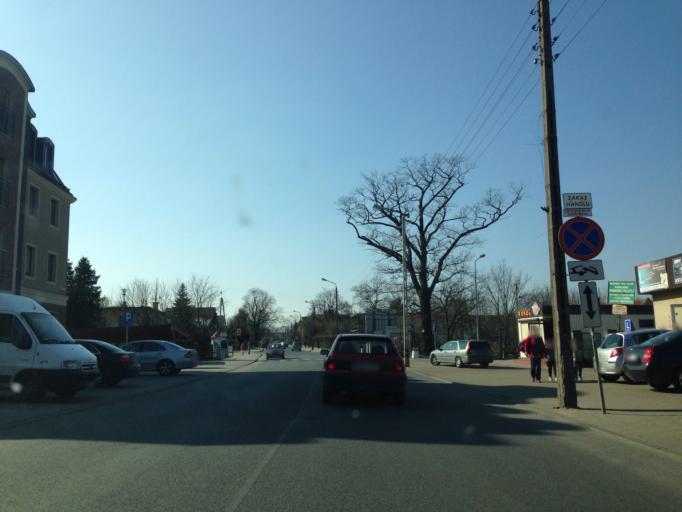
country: PL
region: Lower Silesian Voivodeship
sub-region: Powiat olesnicki
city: Olesnica
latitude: 51.2124
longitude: 17.3740
